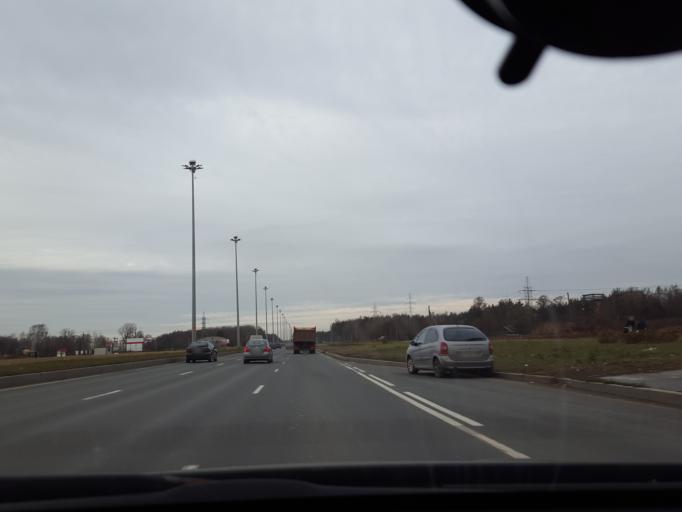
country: RU
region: Leningrad
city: Untolovo
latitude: 60.0414
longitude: 30.2404
